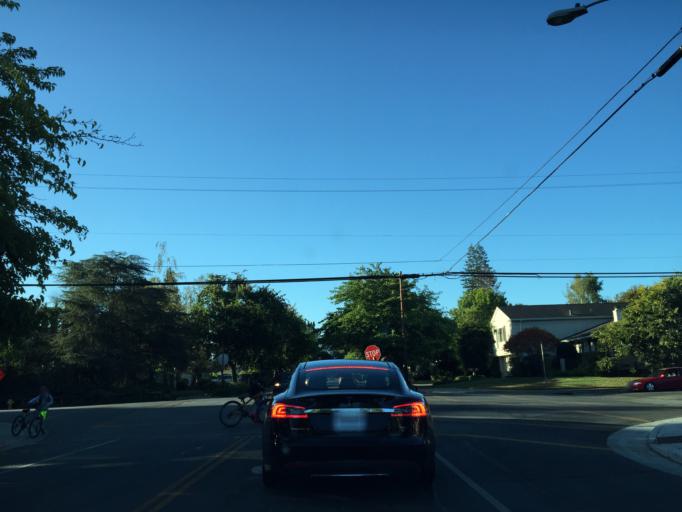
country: US
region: California
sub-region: Santa Clara County
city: Los Altos
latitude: 37.3925
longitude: -122.1209
